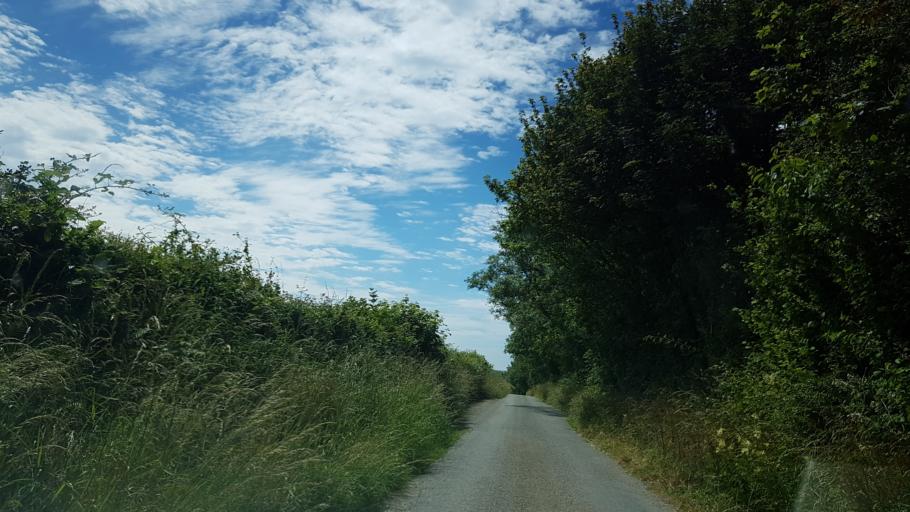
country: GB
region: Wales
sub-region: Pembrokeshire
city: Wiston
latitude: 51.8277
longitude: -4.9014
